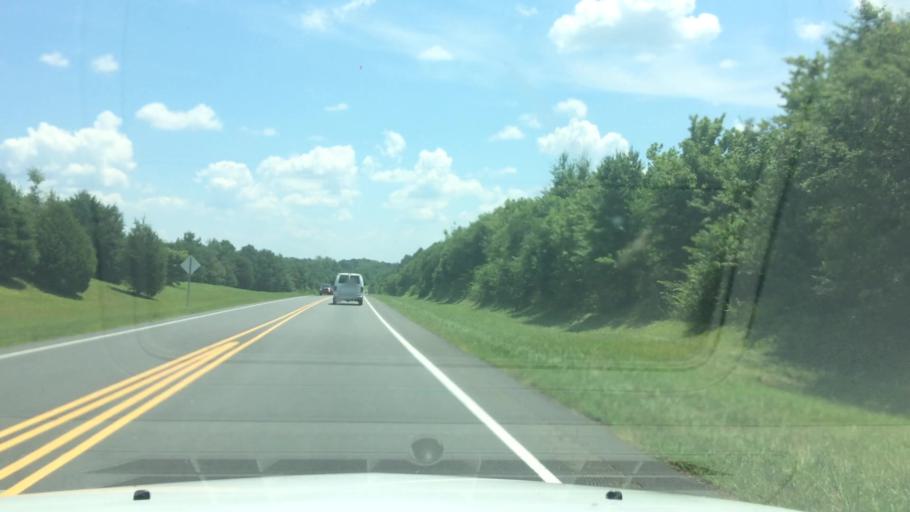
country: US
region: North Carolina
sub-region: Alexander County
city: Stony Point
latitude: 35.8504
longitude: -81.0371
